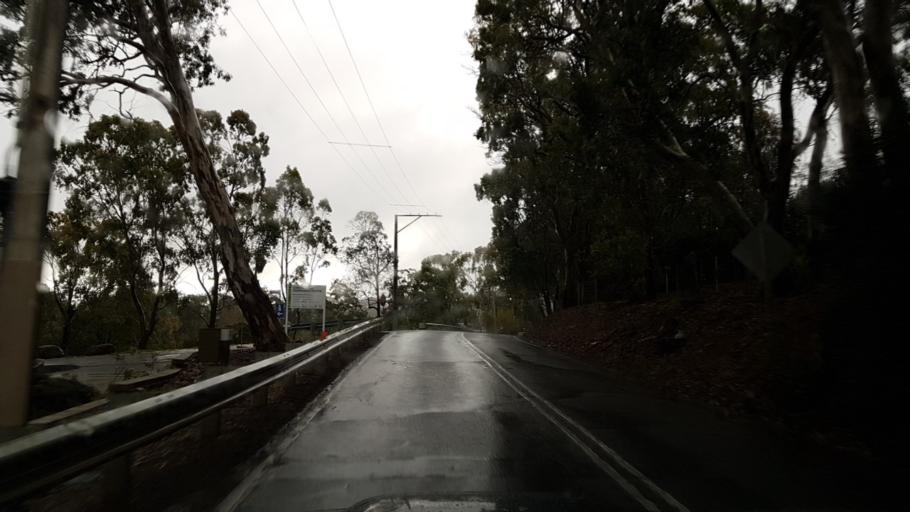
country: AU
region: South Australia
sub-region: Onkaparinga
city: Craigburn Farm
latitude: -35.0516
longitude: 138.6206
